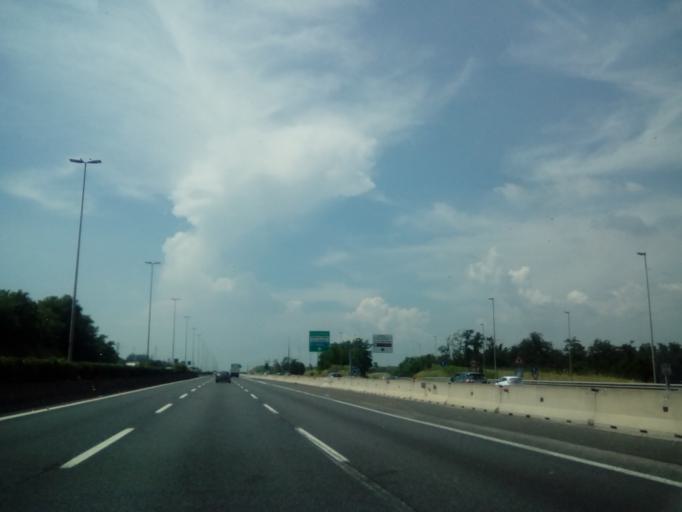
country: IT
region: Latium
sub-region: Citta metropolitana di Roma Capitale
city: Colle Verde
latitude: 41.9762
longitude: 12.5416
